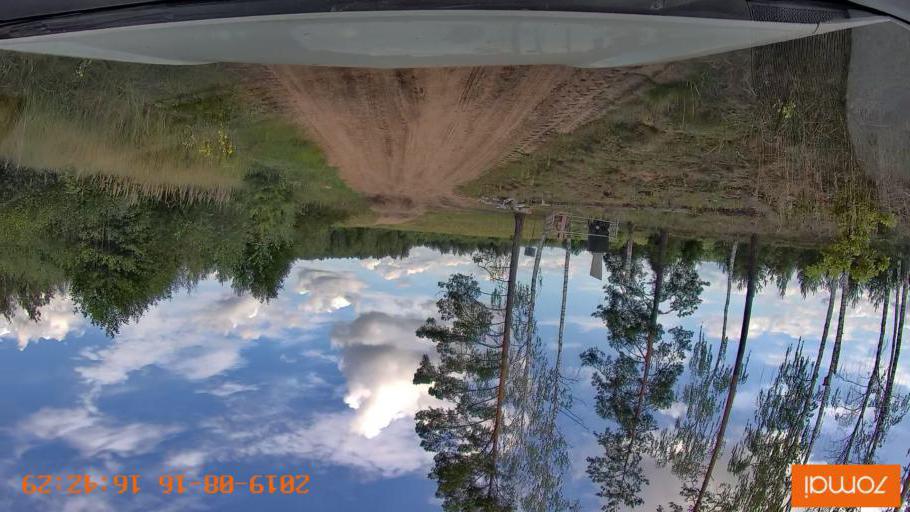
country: BY
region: Mogilev
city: Asipovichy
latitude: 53.2409
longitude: 28.7767
